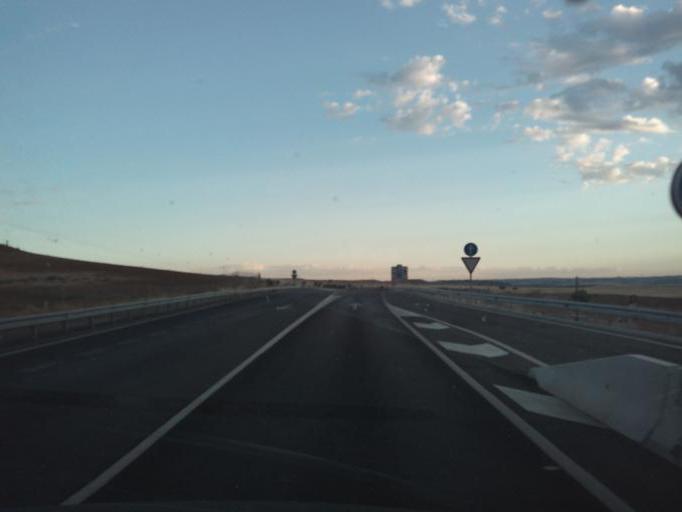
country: ES
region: Madrid
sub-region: Provincia de Madrid
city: Cobena
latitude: 40.5755
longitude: -3.5093
